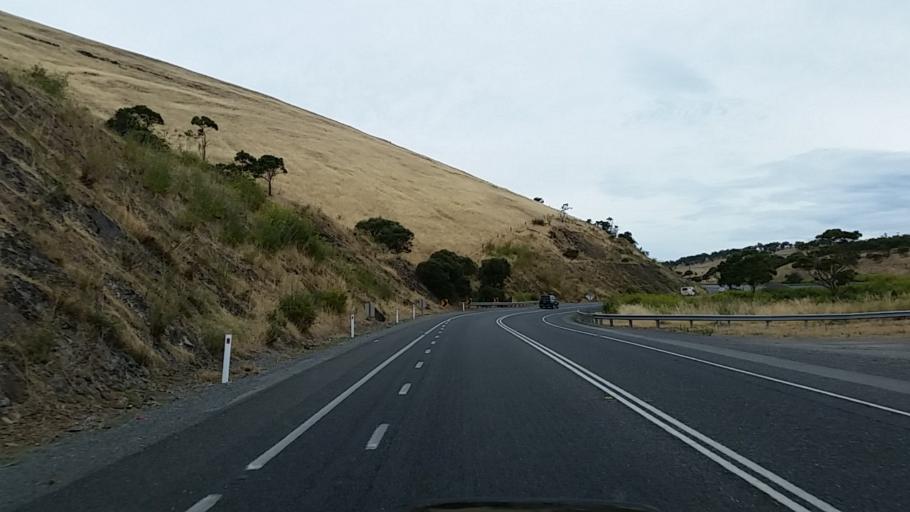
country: AU
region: South Australia
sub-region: Onkaparinga
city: Port Willunga
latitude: -35.3597
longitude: 138.4531
